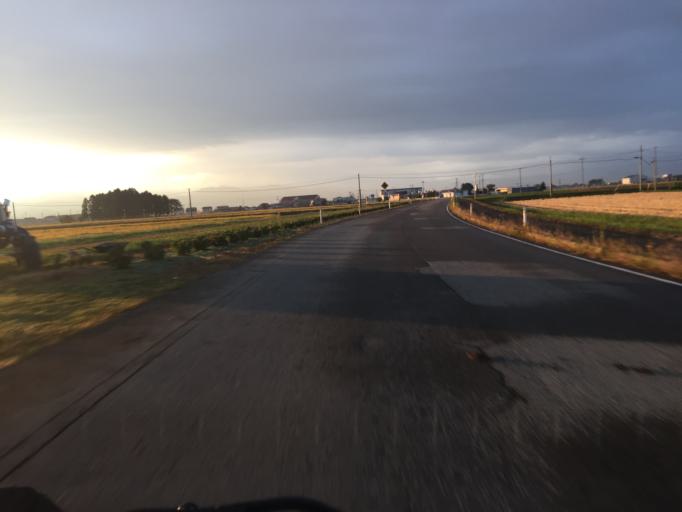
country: JP
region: Fukushima
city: Kitakata
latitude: 37.5596
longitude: 139.8904
